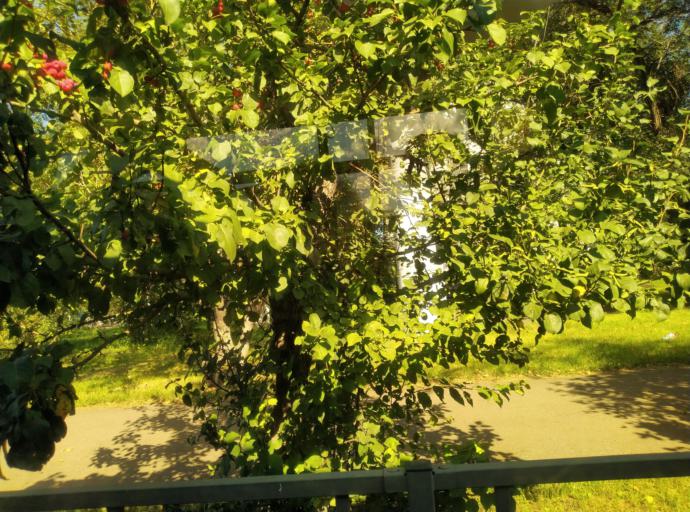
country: RU
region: Krasnoyarskiy
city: Krasnoyarsk
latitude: 55.9781
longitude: 92.8565
